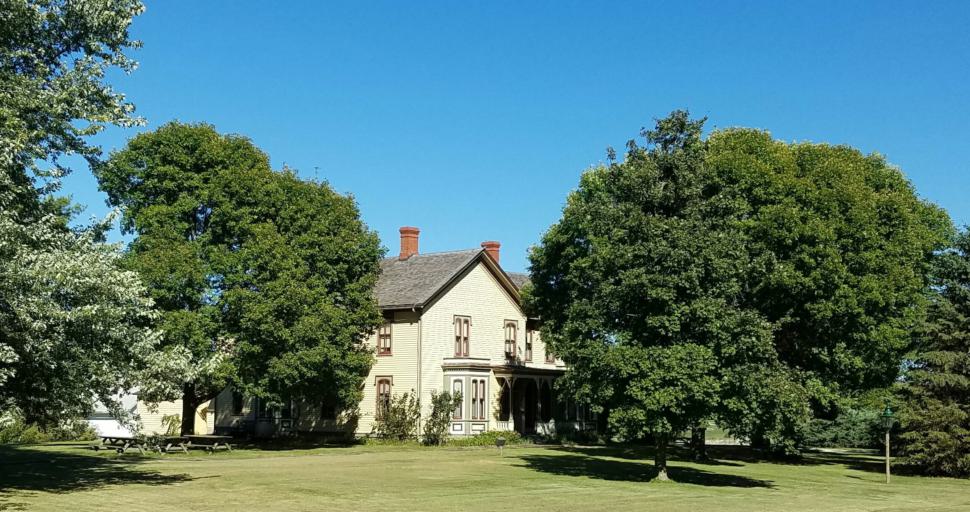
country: US
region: Iowa
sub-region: Decatur County
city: Lamoni
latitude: 40.6237
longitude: -93.9531
